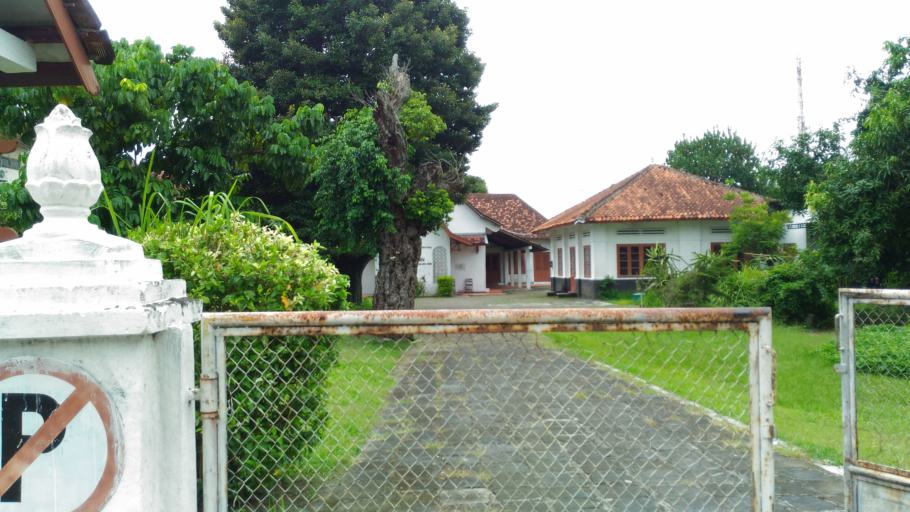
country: ID
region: Daerah Istimewa Yogyakarta
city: Yogyakarta
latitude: -7.8097
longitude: 110.3772
